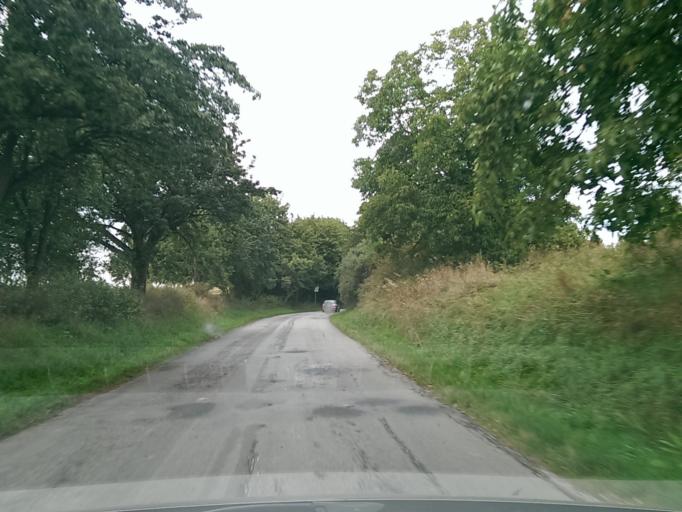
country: CZ
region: Central Bohemia
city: Knezmost
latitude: 50.5104
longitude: 15.0230
